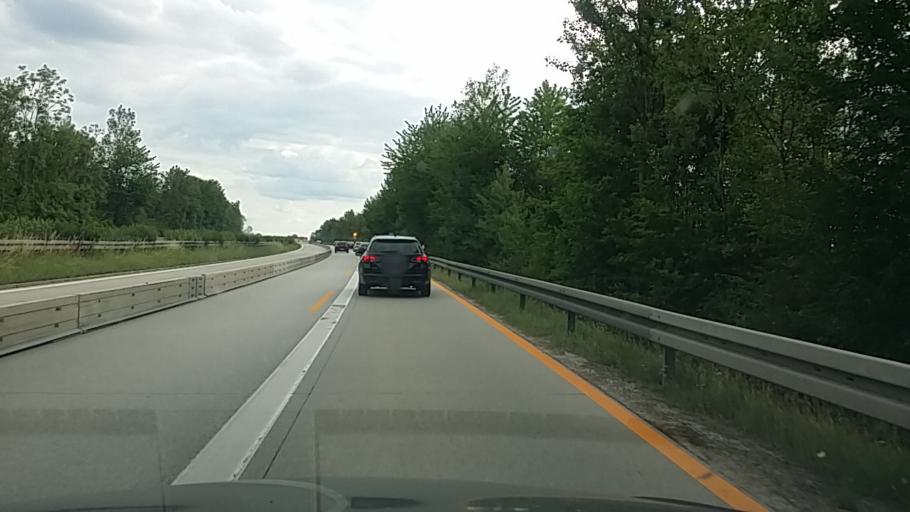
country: DE
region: Bavaria
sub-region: Lower Bavaria
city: Bruckberg
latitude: 48.4999
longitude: 12.0078
